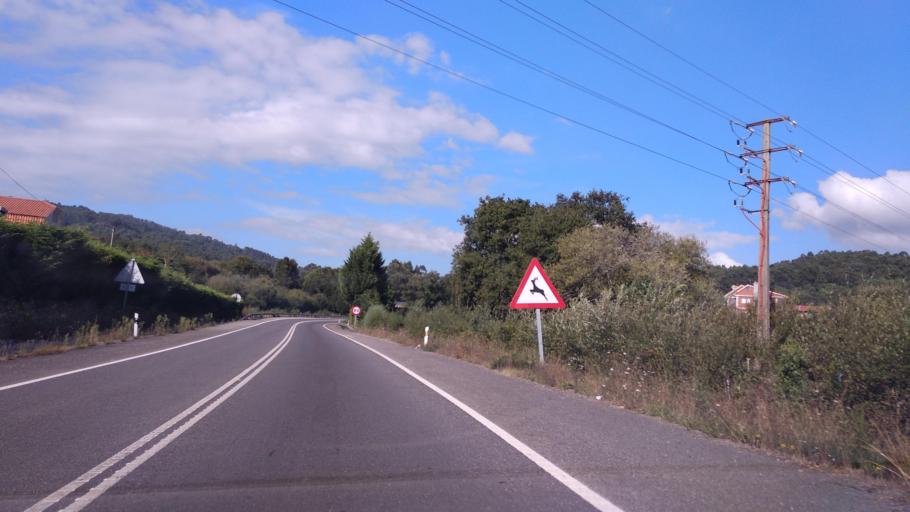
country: ES
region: Galicia
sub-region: Provincia de Pontevedra
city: Cangas
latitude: 42.2688
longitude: -8.7653
